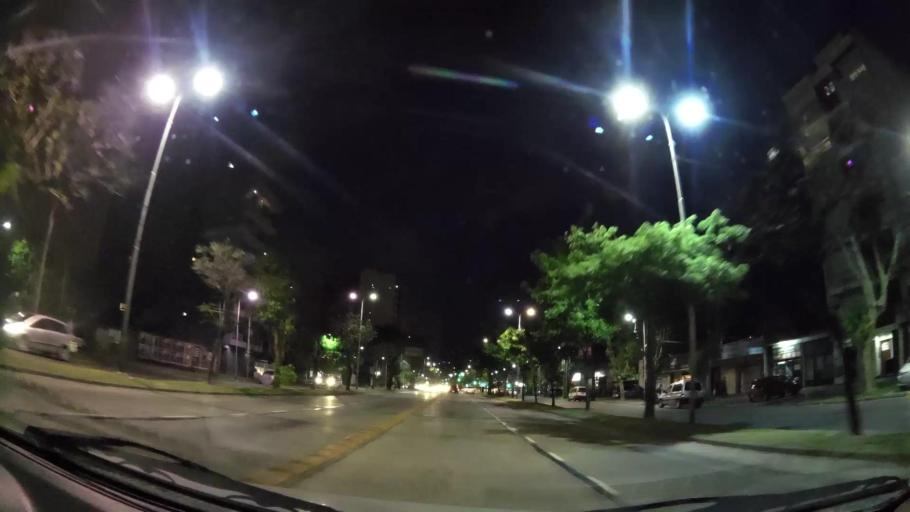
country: AR
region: Buenos Aires
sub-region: Partido de Quilmes
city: Quilmes
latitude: -34.7067
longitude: -58.3146
